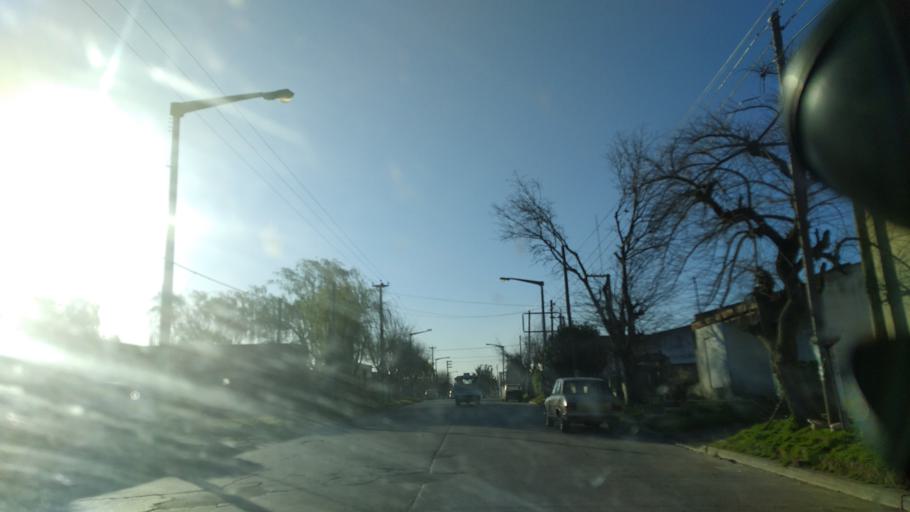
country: AR
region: Buenos Aires
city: Necochea
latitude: -38.5599
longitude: -58.7134
